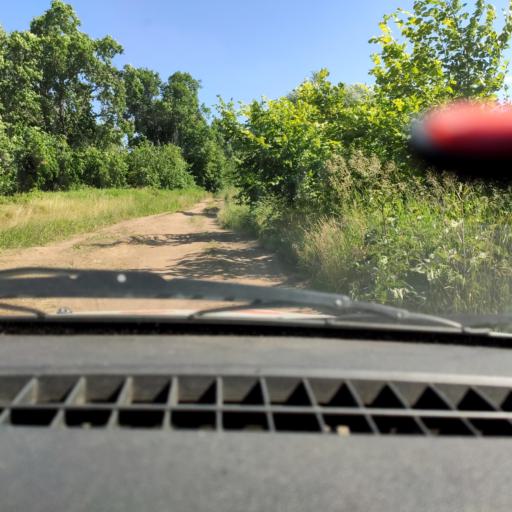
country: RU
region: Bashkortostan
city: Sterlitamak
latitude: 53.7466
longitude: 56.0810
